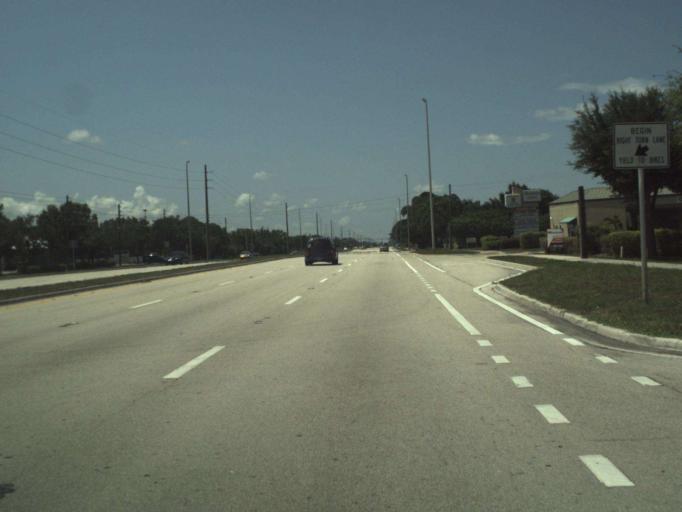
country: US
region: Florida
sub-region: Saint Lucie County
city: Port Saint Lucie
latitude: 27.2808
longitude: -80.2938
